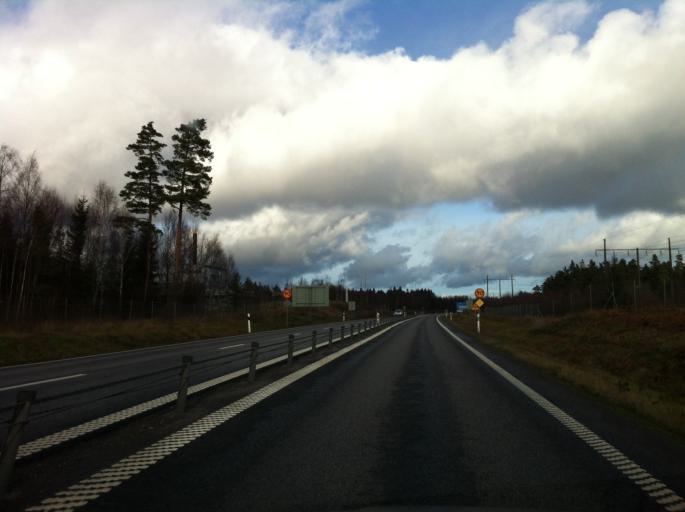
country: SE
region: Kronoberg
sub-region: Almhults Kommun
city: AElmhult
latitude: 56.5107
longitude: 14.1303
